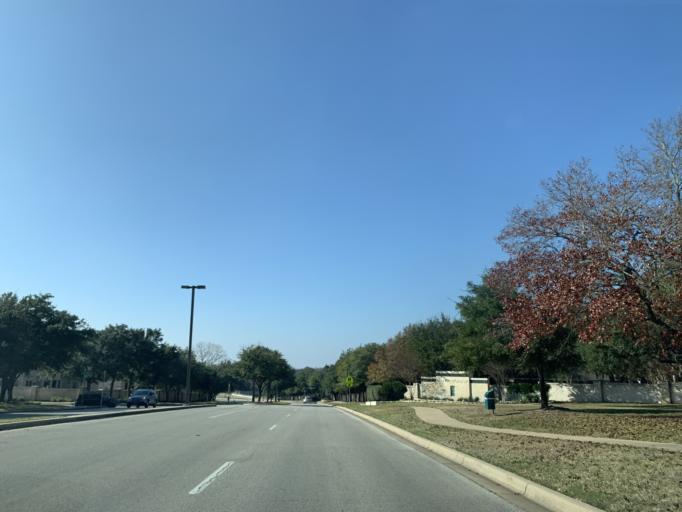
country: US
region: Texas
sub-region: Travis County
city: Windemere
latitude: 30.5083
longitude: -97.6186
